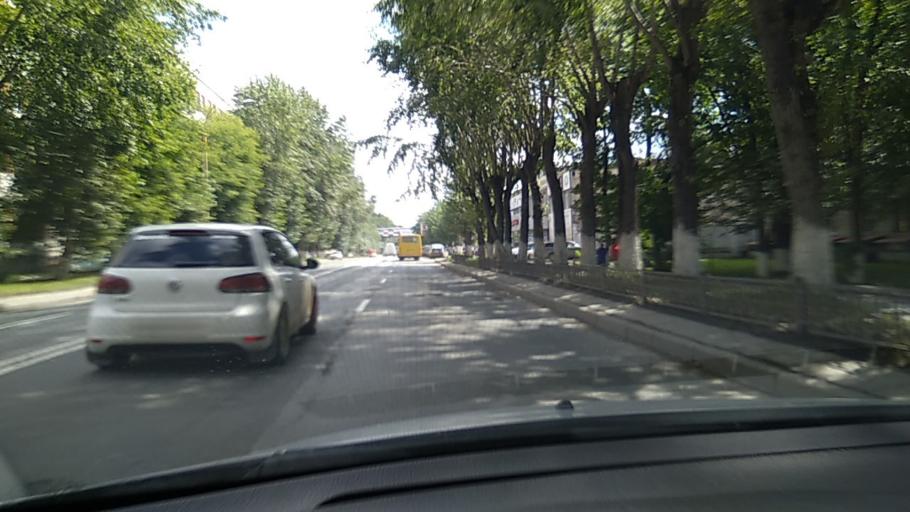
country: RU
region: Sverdlovsk
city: Yekaterinburg
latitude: 56.8248
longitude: 60.6464
